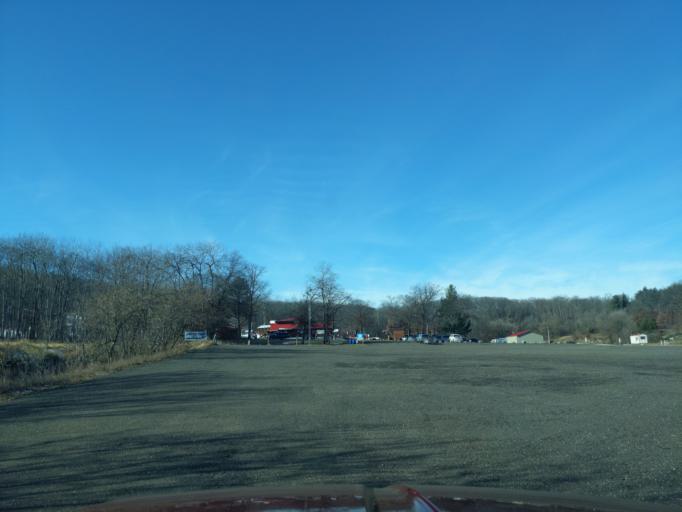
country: US
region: Wisconsin
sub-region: Waushara County
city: Silver Lake
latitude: 44.1213
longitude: -89.1791
